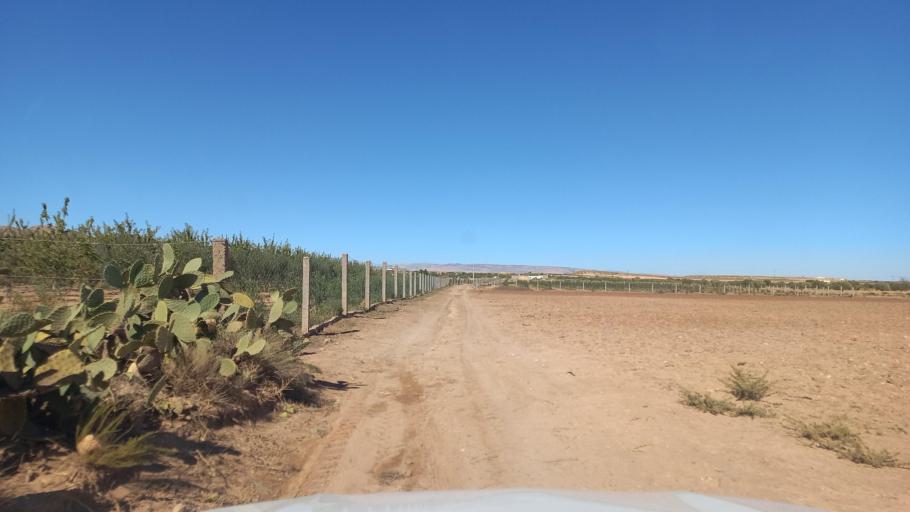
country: TN
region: Al Qasrayn
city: Sbiba
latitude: 35.3910
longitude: 9.0819
